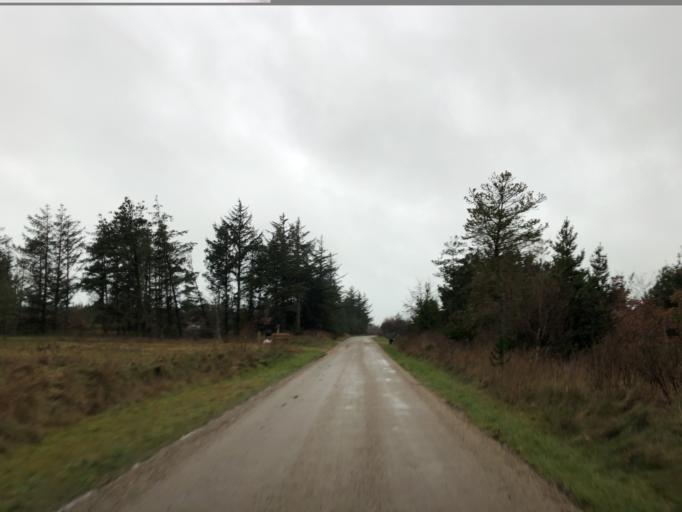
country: DK
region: Central Jutland
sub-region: Holstebro Kommune
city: Ulfborg
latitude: 56.2787
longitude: 8.1480
